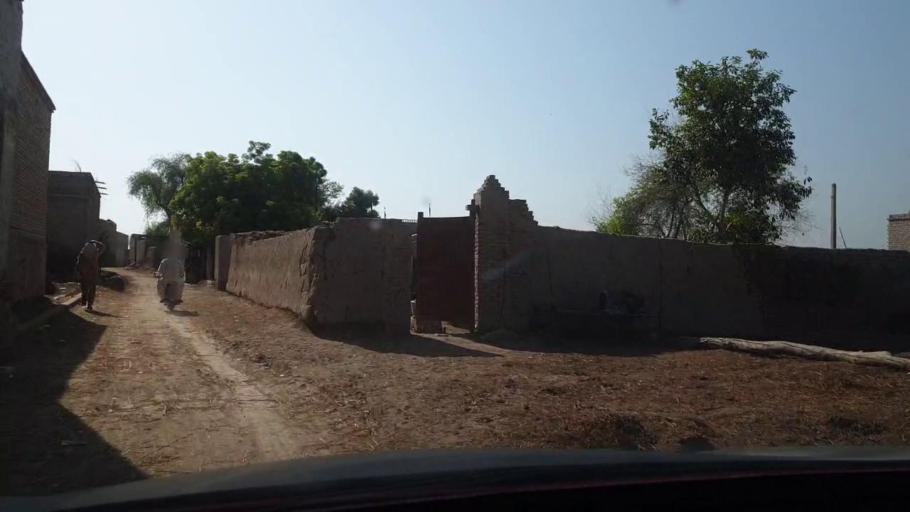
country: PK
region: Sindh
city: Nasirabad
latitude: 27.3853
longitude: 67.8721
